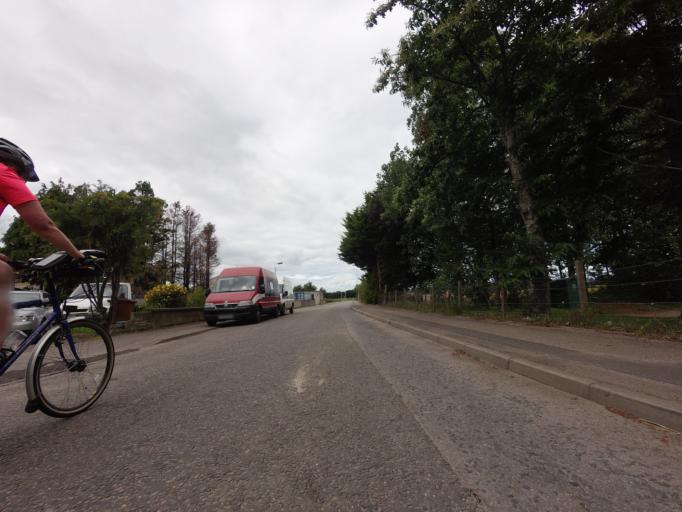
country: GB
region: Scotland
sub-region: Moray
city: Forres
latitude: 57.6132
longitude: -3.6218
